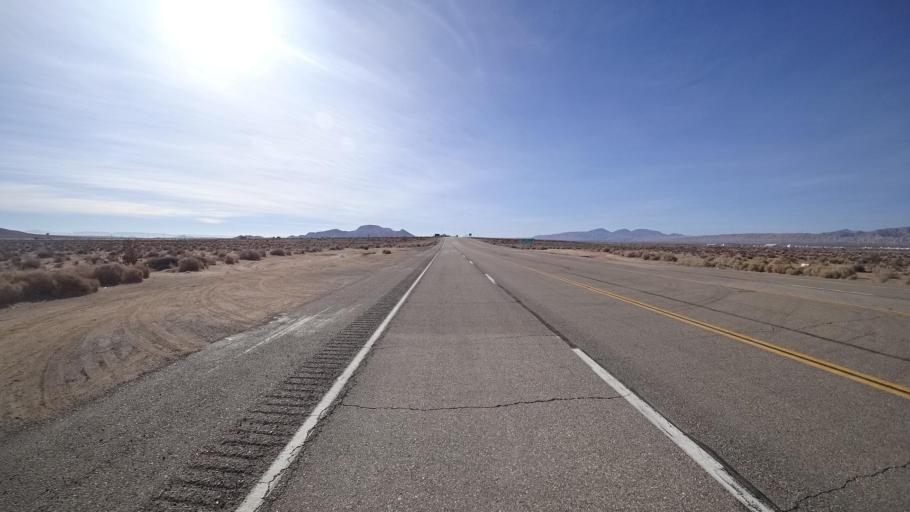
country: US
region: California
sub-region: Kern County
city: Mojave
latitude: 35.0404
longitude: -118.1014
